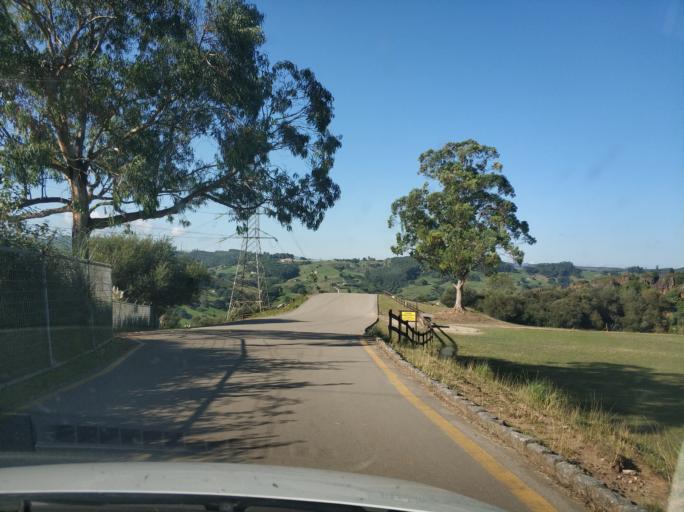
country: ES
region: Cantabria
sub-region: Provincia de Cantabria
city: Penagos
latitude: 43.3454
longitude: -3.8486
